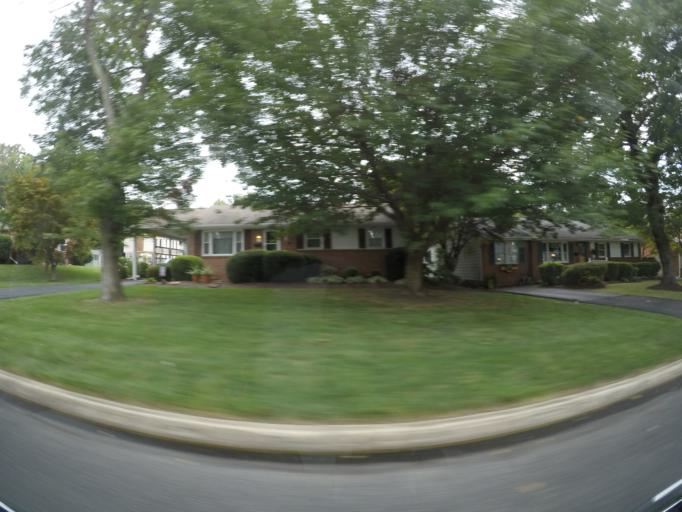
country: US
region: Maryland
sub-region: Harford County
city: North Bel Air
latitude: 39.5346
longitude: -76.3557
